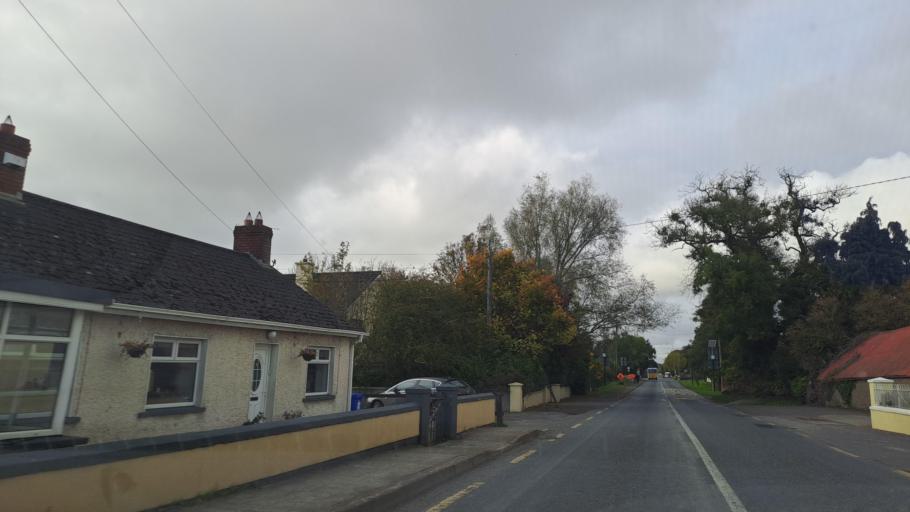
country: IE
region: Leinster
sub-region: An Mhi
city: Navan
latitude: 53.7325
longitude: -6.7098
